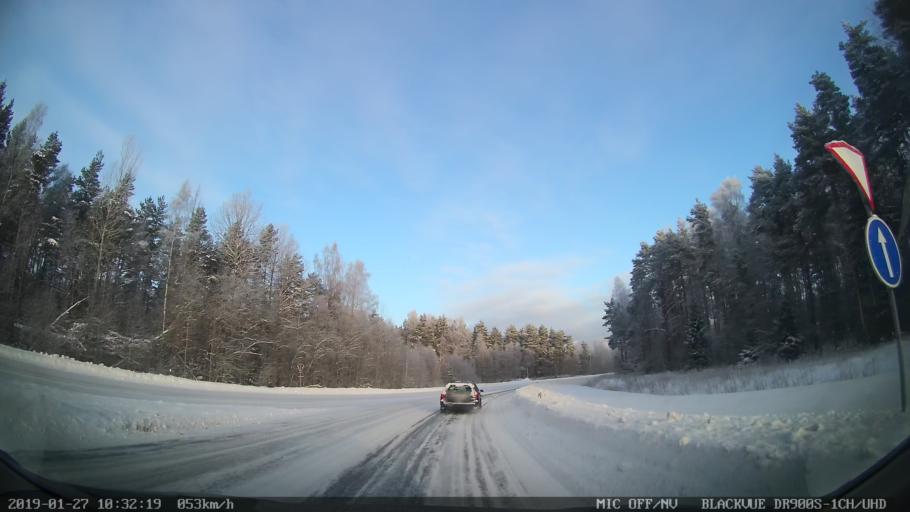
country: EE
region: Harju
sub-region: Raasiku vald
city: Raasiku
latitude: 59.4396
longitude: 25.1872
